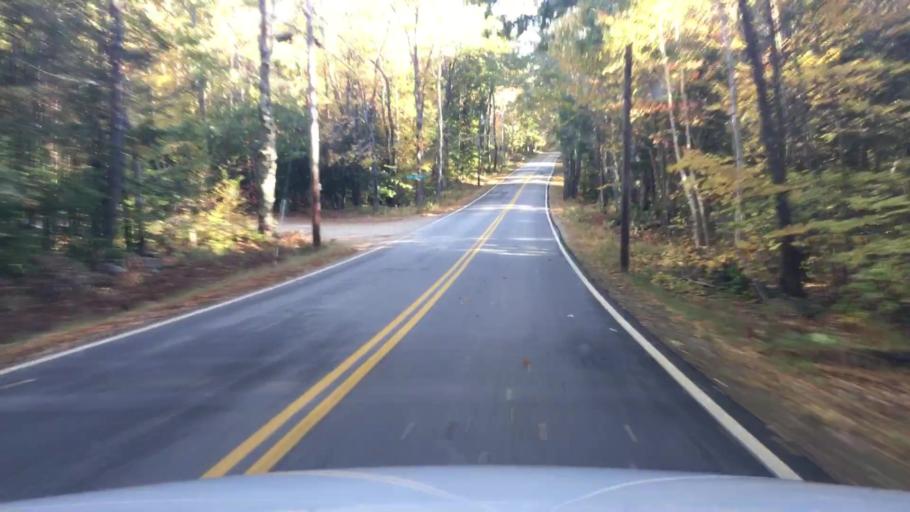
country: US
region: New Hampshire
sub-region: Strafford County
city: Barrington
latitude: 43.1702
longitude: -71.0496
